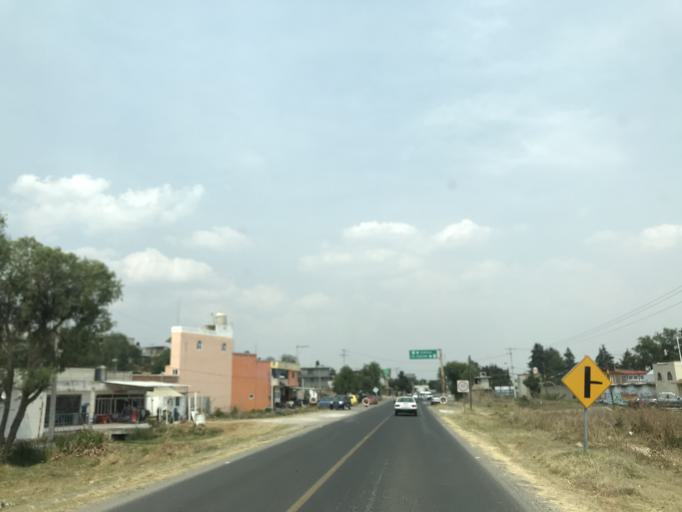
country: MX
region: Tlaxcala
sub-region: Ixtacuixtla de Mariano Matamoros
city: Santa Justina Ecatepec
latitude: 19.3087
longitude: -98.3562
